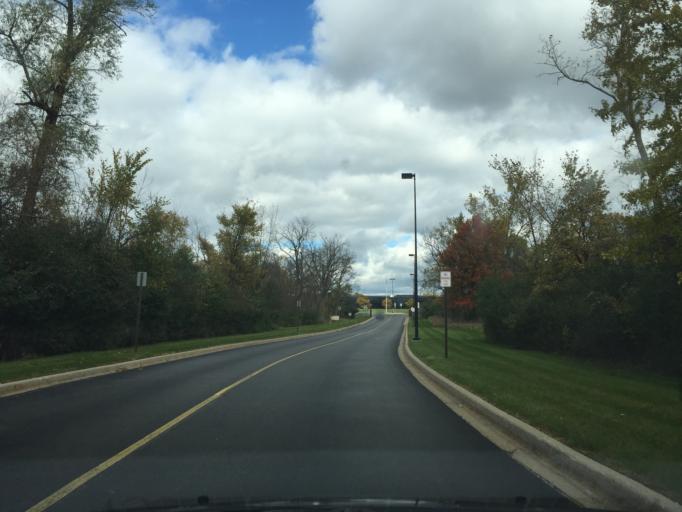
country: US
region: Michigan
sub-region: Oakland County
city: Auburn Hills
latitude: 42.6475
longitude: -83.2347
